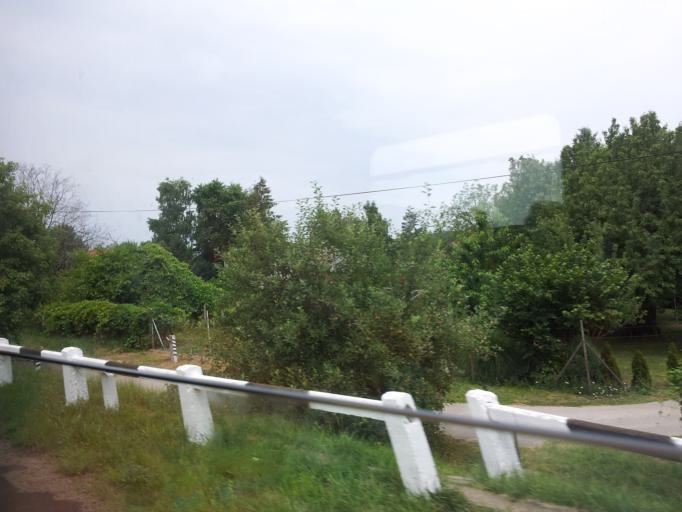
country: HU
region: Veszprem
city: Badacsonytomaj
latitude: 46.7917
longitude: 17.4728
